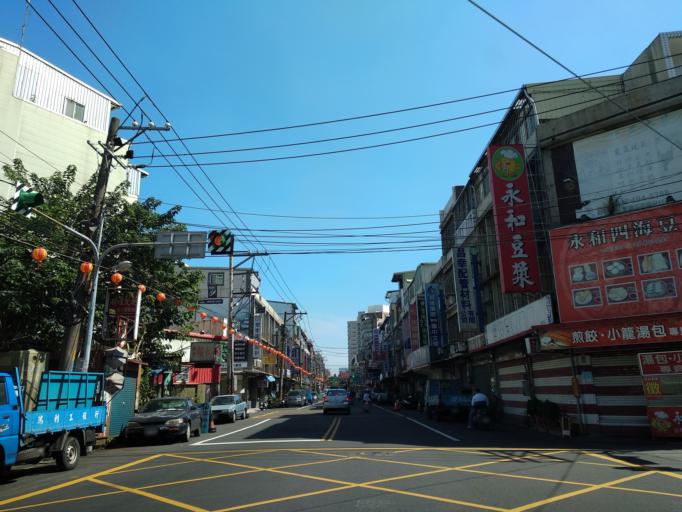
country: TW
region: Taiwan
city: Taoyuan City
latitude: 24.9468
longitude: 121.2118
